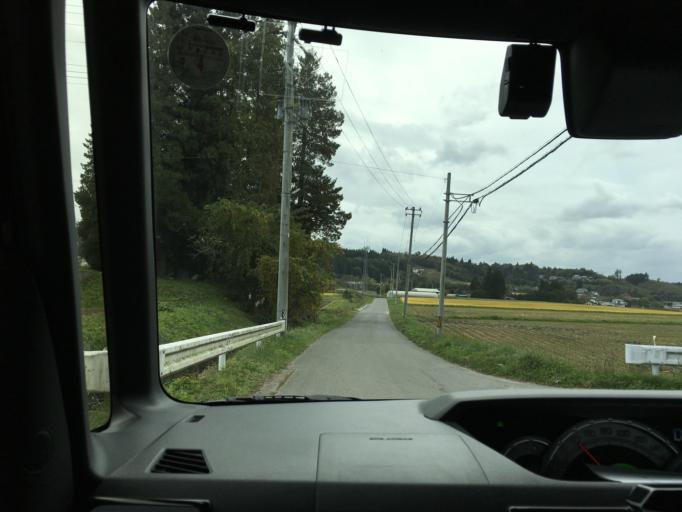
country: JP
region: Iwate
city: Ichinoseki
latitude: 39.0201
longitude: 141.3498
